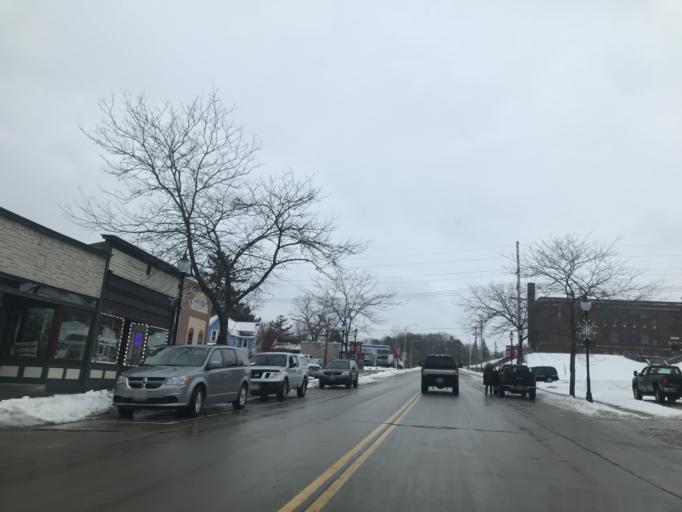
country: US
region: Wisconsin
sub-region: Door County
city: Sturgeon Bay
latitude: 44.8275
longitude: -87.3845
